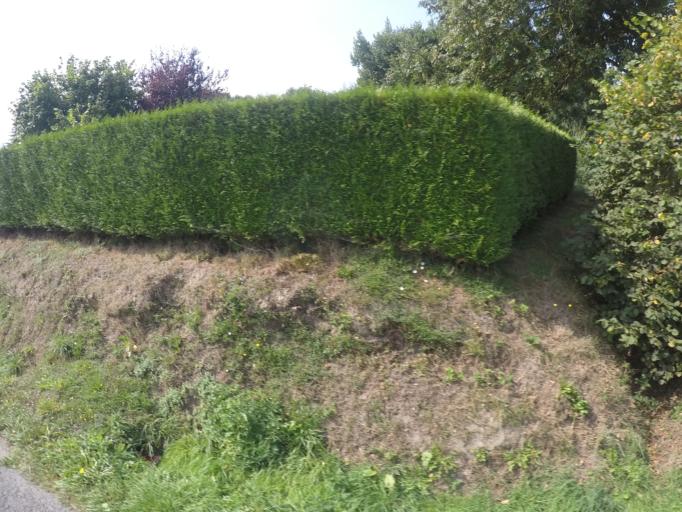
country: FR
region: Brittany
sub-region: Departement des Cotes-d'Armor
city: Tremuson
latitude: 48.5182
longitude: -2.8783
